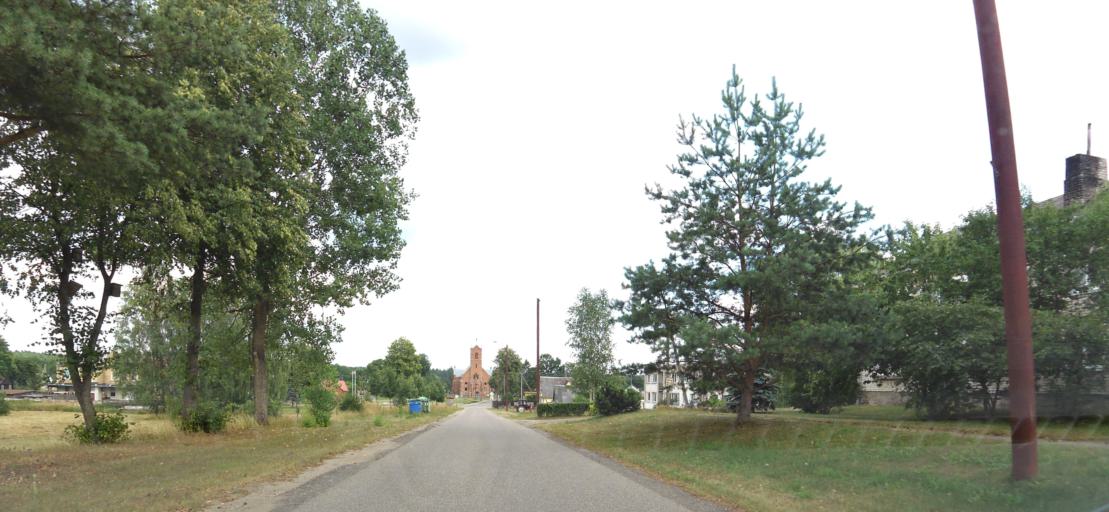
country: LT
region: Alytaus apskritis
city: Varena
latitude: 54.2157
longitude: 24.4152
